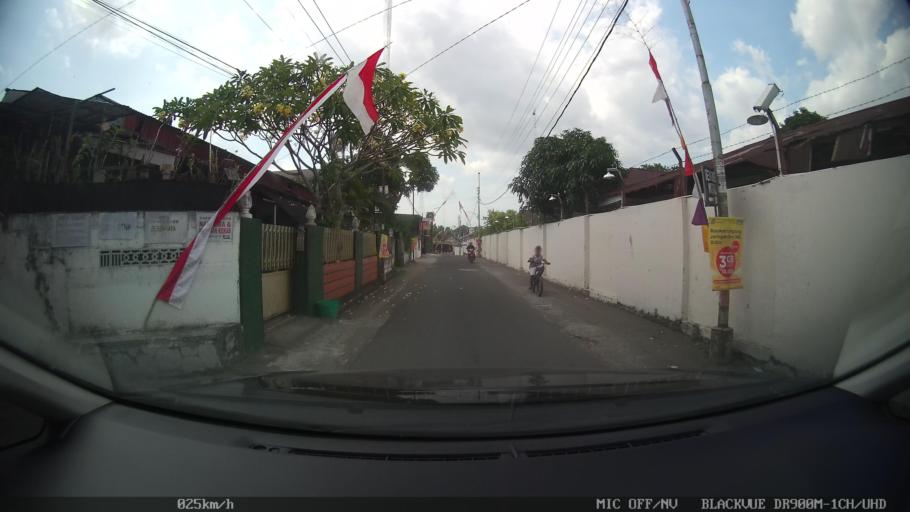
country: ID
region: Daerah Istimewa Yogyakarta
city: Gamping Lor
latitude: -7.8019
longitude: 110.3385
